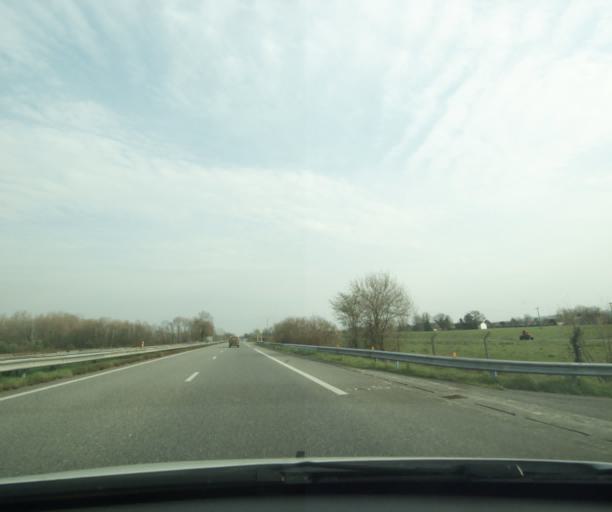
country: FR
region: Aquitaine
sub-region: Departement des Pyrenees-Atlantiques
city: Orthez
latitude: 43.4653
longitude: -0.7339
